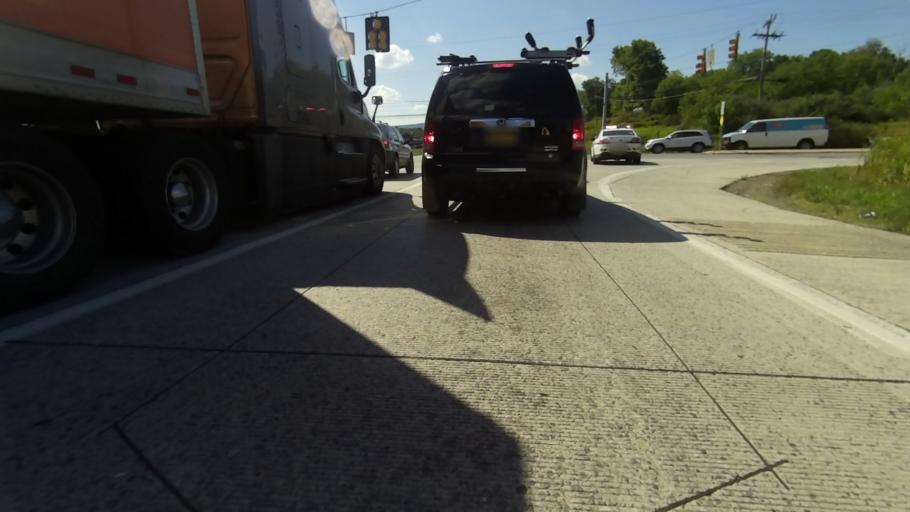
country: US
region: Pennsylvania
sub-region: Blair County
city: Greenwood
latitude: 40.5658
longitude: -78.3372
